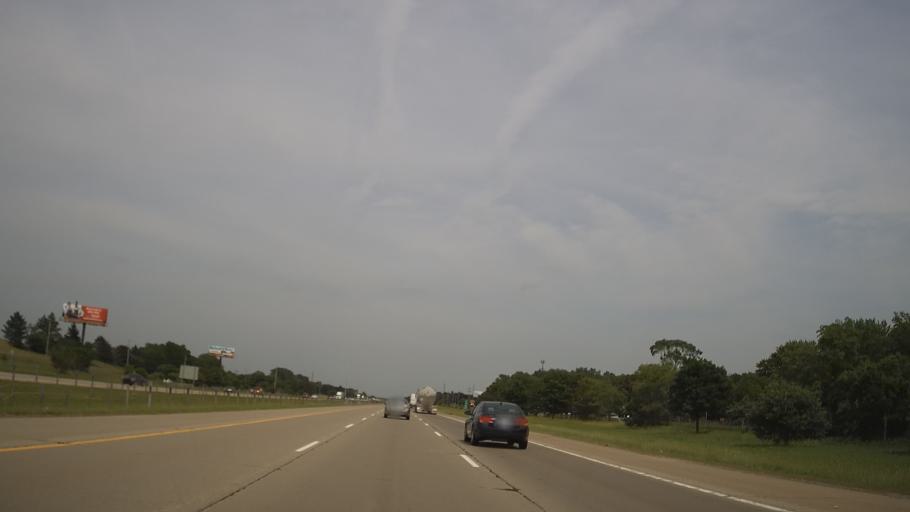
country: US
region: Michigan
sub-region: Wayne County
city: Belleville
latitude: 42.2187
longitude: -83.5307
